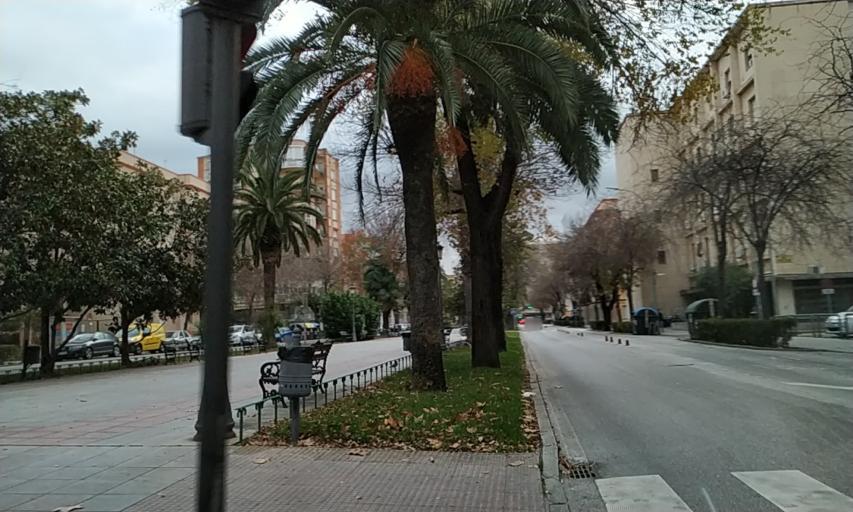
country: ES
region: Extremadura
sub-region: Provincia de Badajoz
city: Badajoz
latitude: 38.8765
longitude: -6.9765
